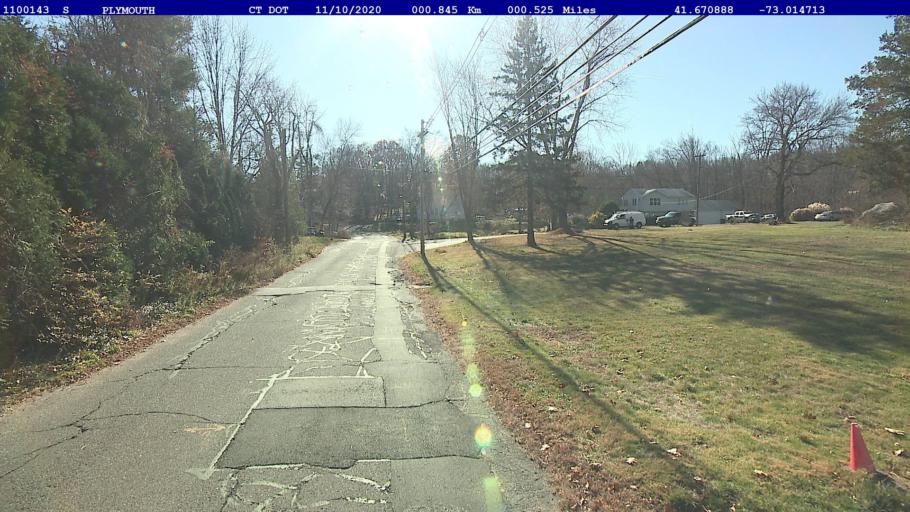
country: US
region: Connecticut
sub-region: Litchfield County
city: Terryville
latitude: 41.6709
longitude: -73.0147
